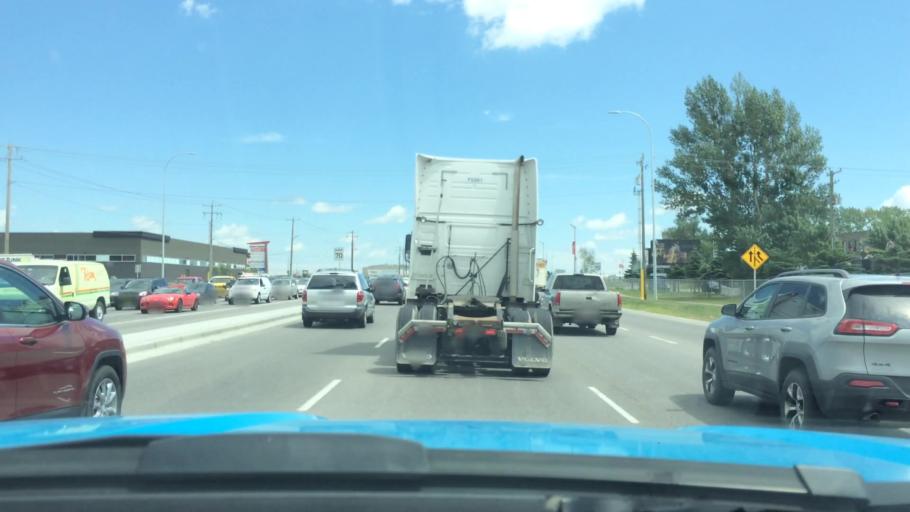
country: CA
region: Alberta
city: Calgary
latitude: 51.0960
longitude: -114.0332
